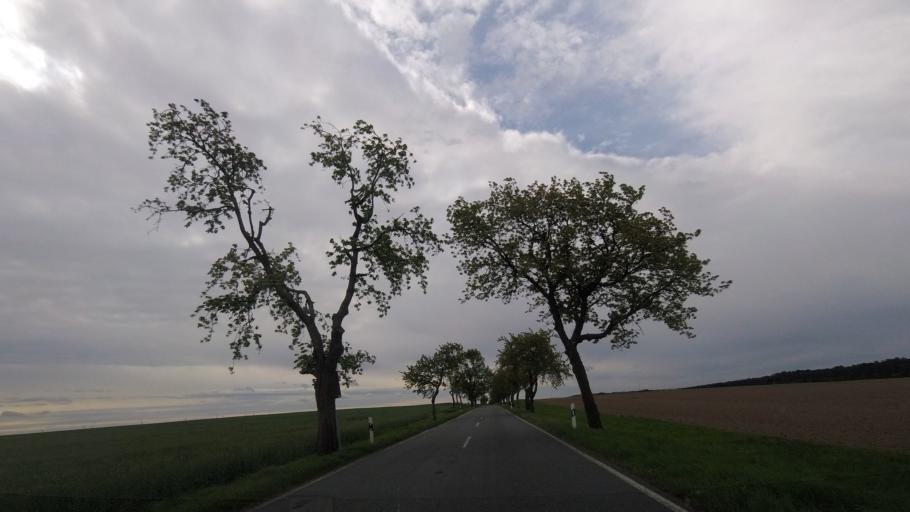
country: DE
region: Brandenburg
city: Dahme
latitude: 51.9130
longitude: 13.4007
